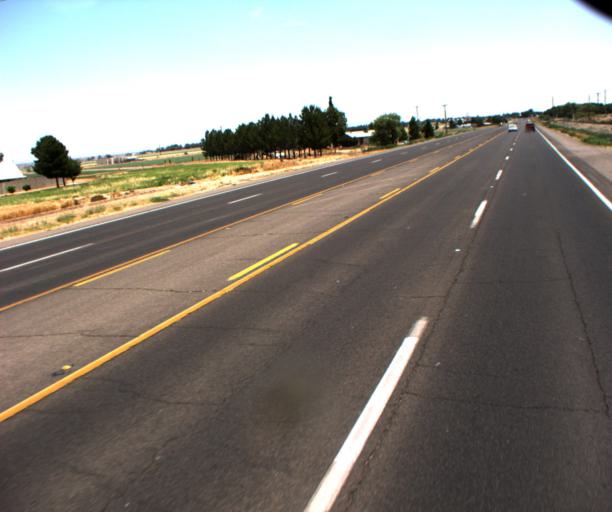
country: US
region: Arizona
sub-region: Graham County
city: Thatcher
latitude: 32.8608
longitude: -109.7861
